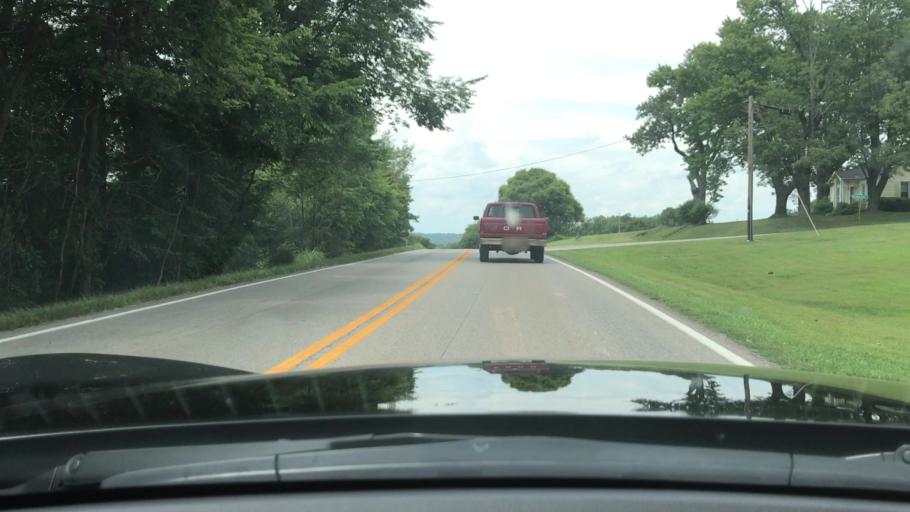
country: US
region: Kentucky
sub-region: Hart County
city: Horse Cave
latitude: 37.1760
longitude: -85.8688
